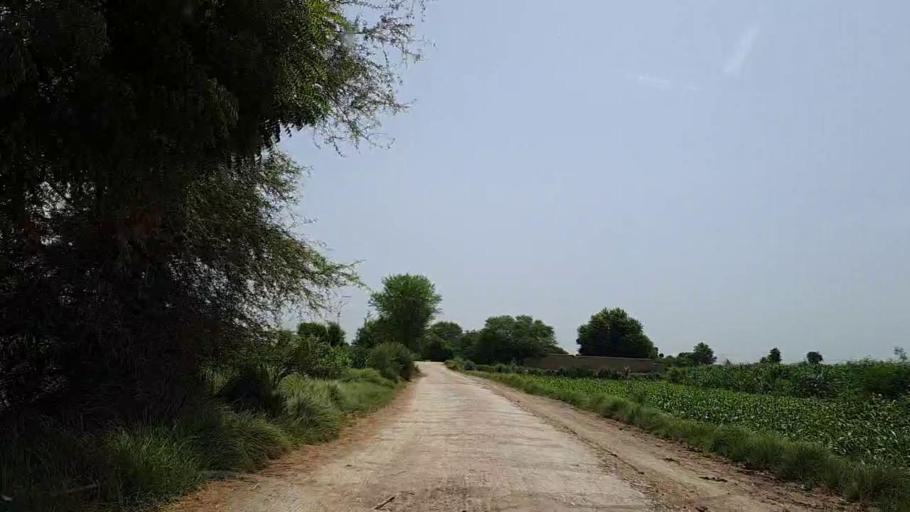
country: PK
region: Sindh
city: Naushahro Firoz
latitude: 26.8423
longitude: 67.9768
